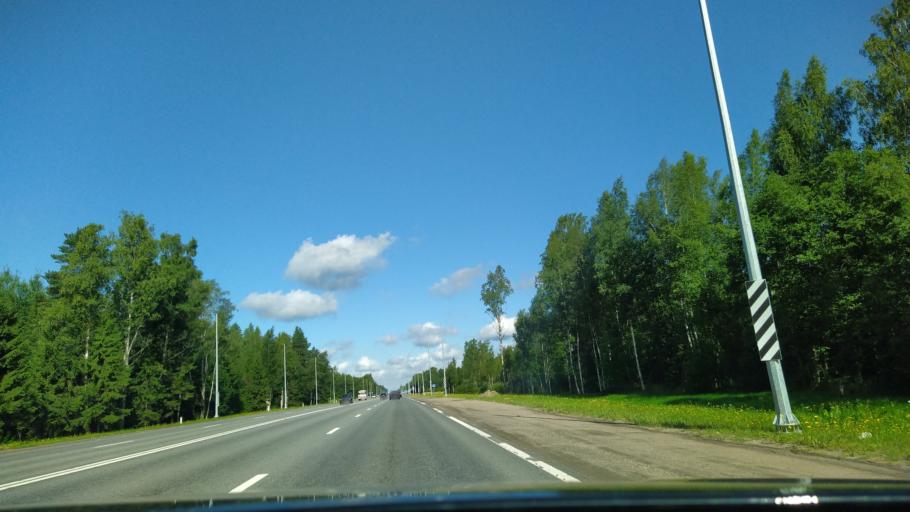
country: RU
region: Leningrad
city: Tosno
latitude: 59.5758
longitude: 30.8138
